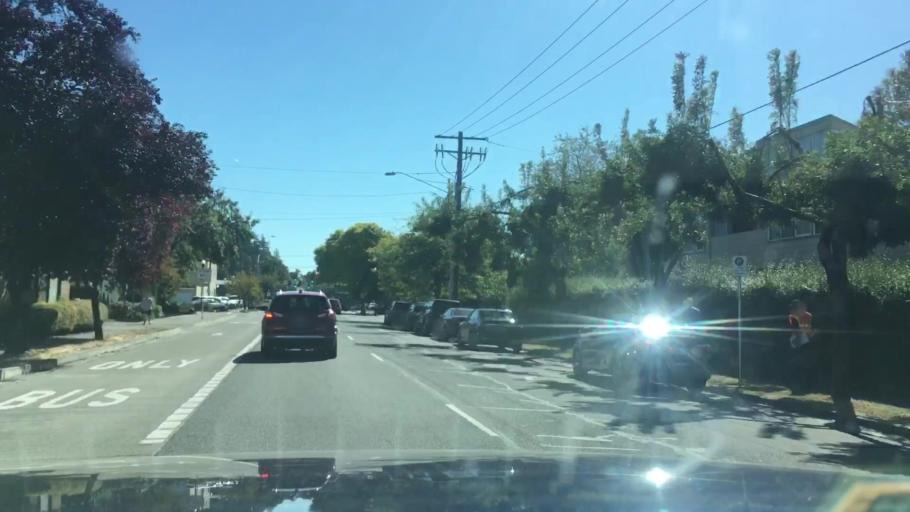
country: US
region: Oregon
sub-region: Lane County
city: Springfield
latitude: 44.0479
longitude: -123.0233
